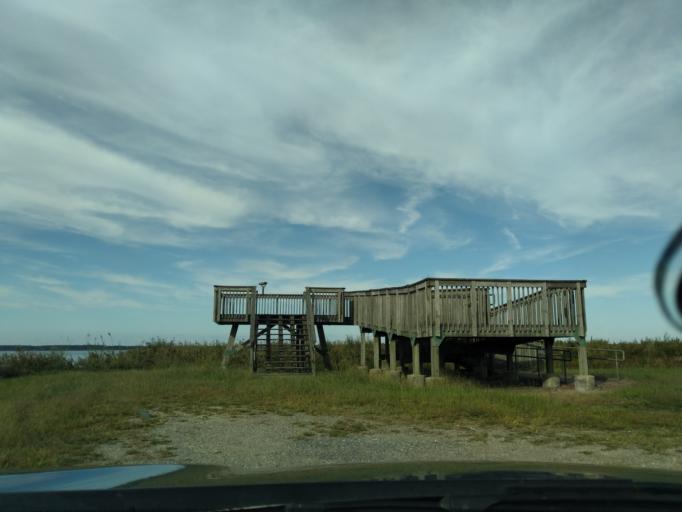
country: US
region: North Carolina
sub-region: Beaufort County
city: Belhaven
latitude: 35.6929
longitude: -76.5421
